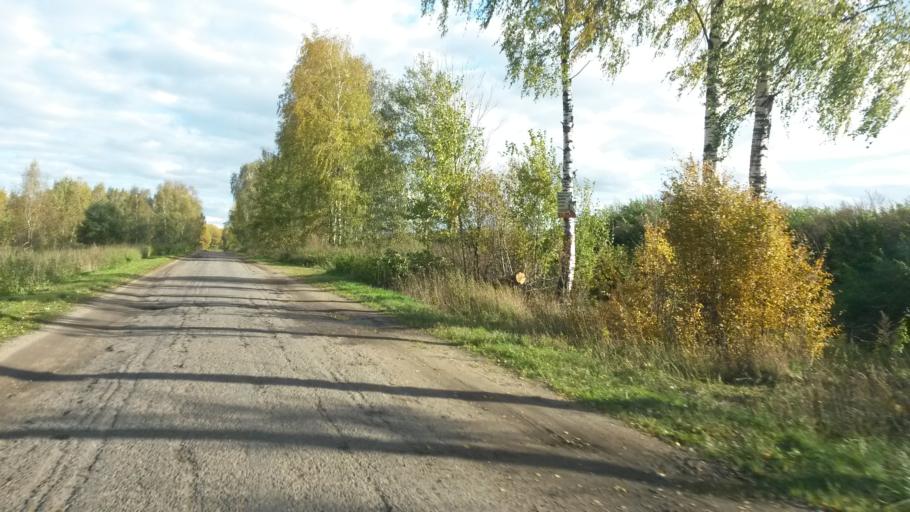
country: RU
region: Jaroslavl
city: Tunoshna
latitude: 57.5253
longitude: 40.0045
